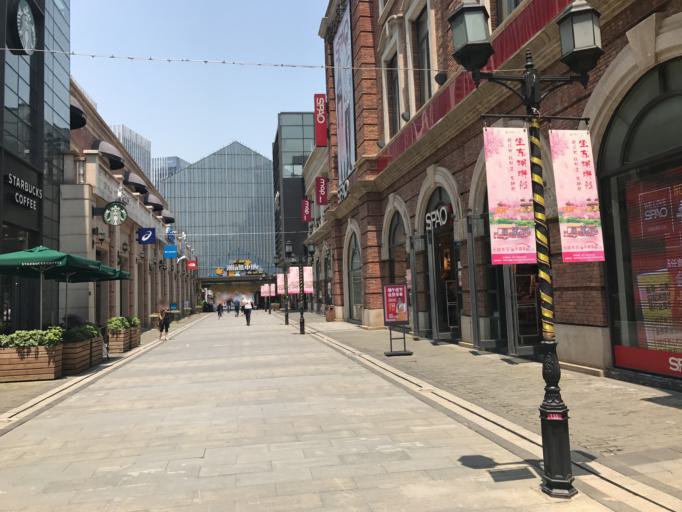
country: CN
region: Hubei
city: Jiang'an
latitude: 30.5602
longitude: 114.3336
